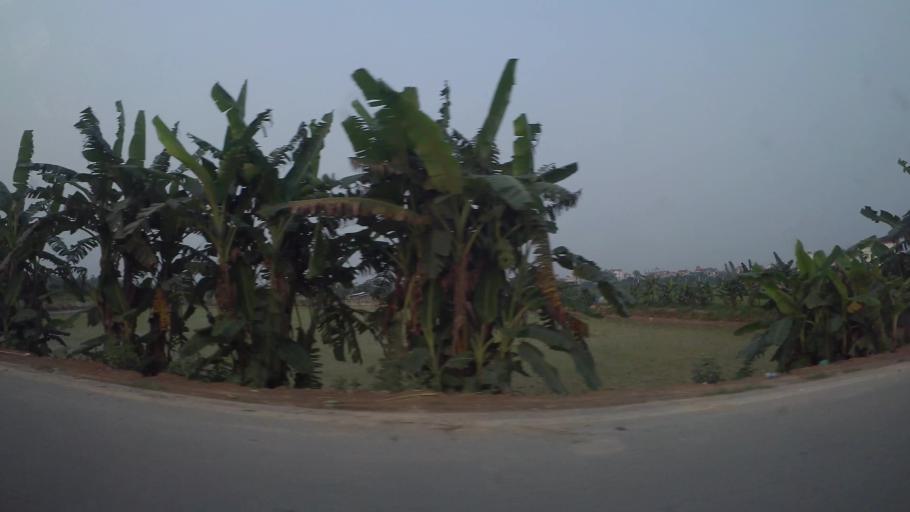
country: VN
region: Ha Noi
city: Kim Bai
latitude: 20.8735
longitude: 105.8029
